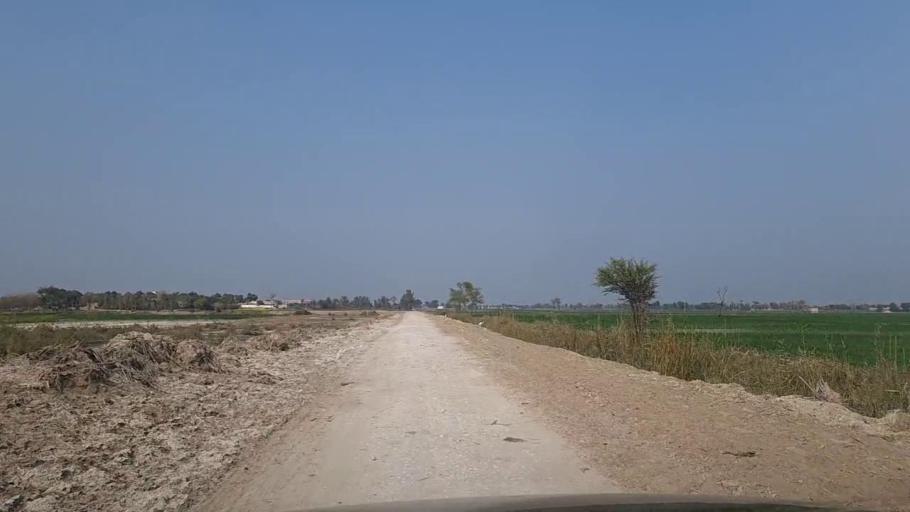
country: PK
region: Sindh
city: Daur
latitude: 26.3889
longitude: 68.4236
